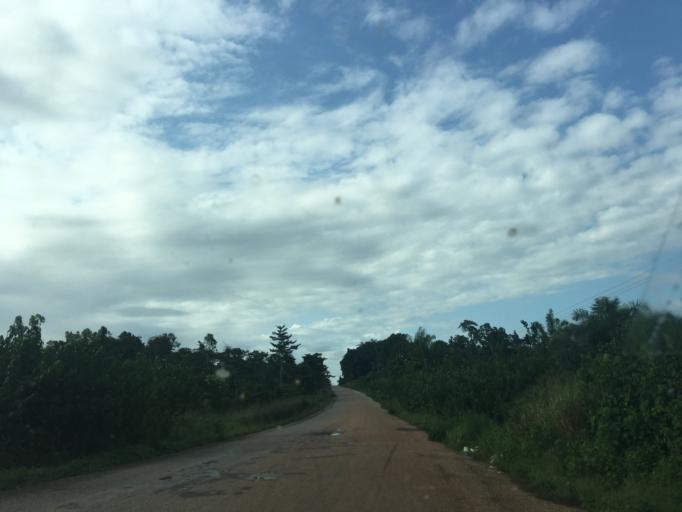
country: GH
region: Western
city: Wassa-Akropong
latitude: 5.9877
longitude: -2.4126
